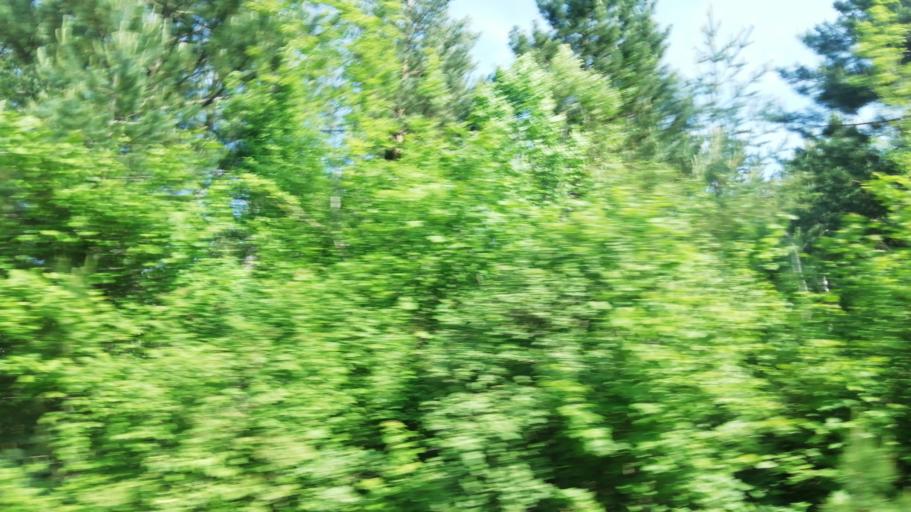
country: TR
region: Karabuk
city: Karabuk
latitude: 41.0831
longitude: 32.5669
